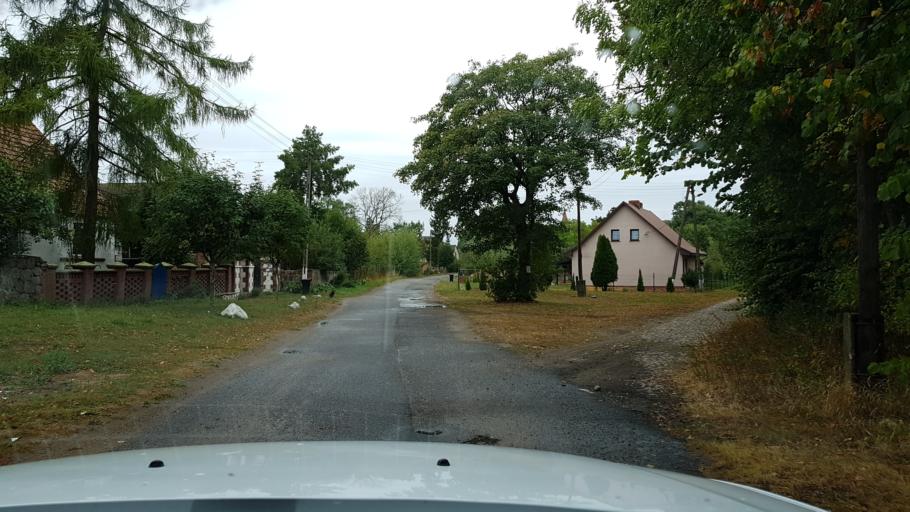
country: PL
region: West Pomeranian Voivodeship
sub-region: Powiat gryfinski
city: Cedynia
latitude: 52.8493
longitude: 14.2946
